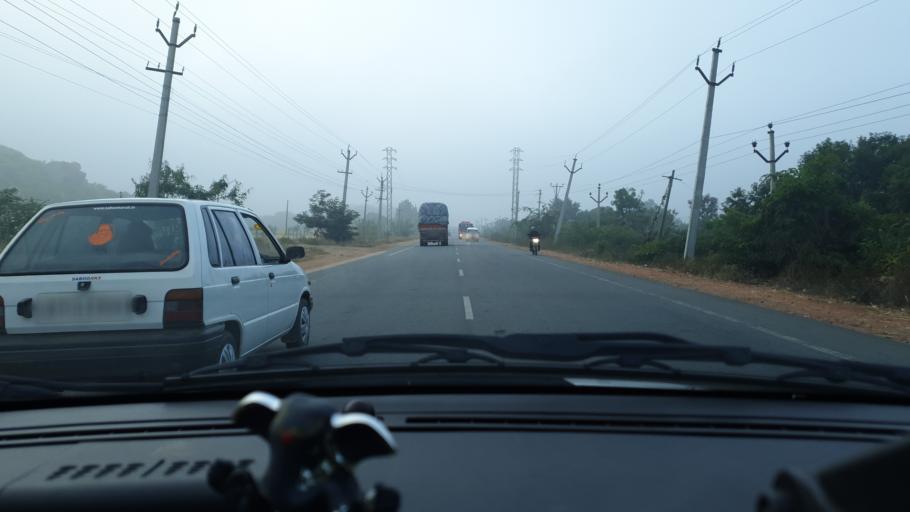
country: IN
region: Telangana
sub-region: Mahbubnagar
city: Farrukhnagar
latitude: 16.8667
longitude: 78.5290
